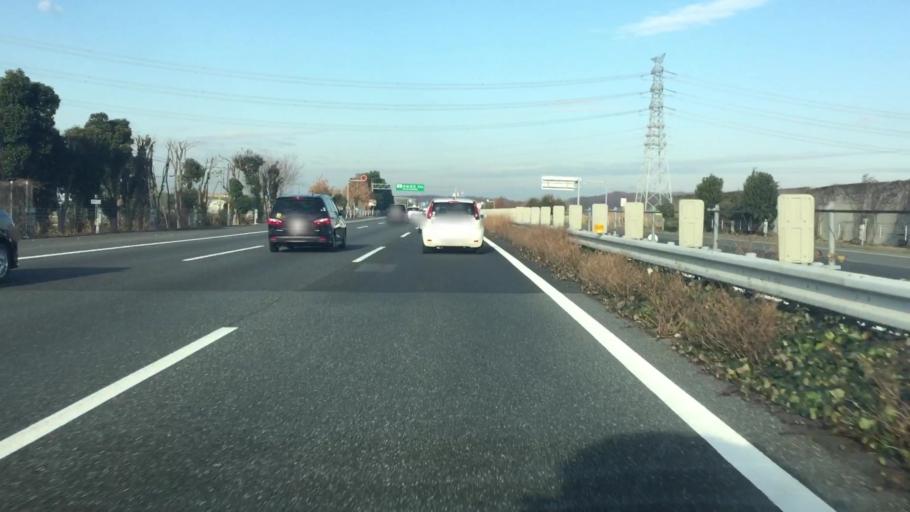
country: JP
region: Saitama
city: Honjo
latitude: 36.2013
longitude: 139.1807
